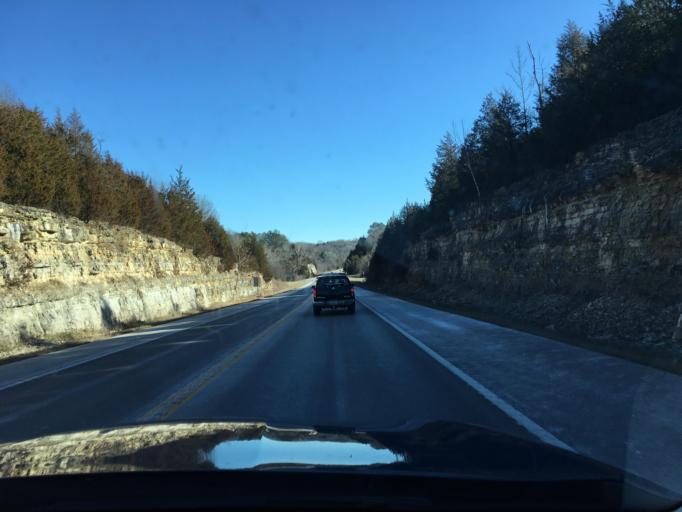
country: US
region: Missouri
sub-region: Jefferson County
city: De Soto
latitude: 38.1385
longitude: -90.4945
